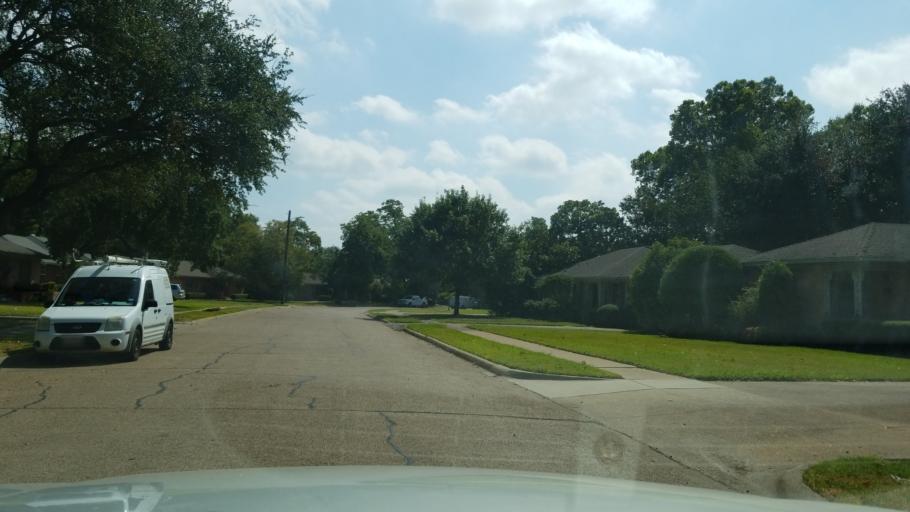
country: US
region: Texas
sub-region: Dallas County
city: Garland
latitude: 32.8959
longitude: -96.6609
